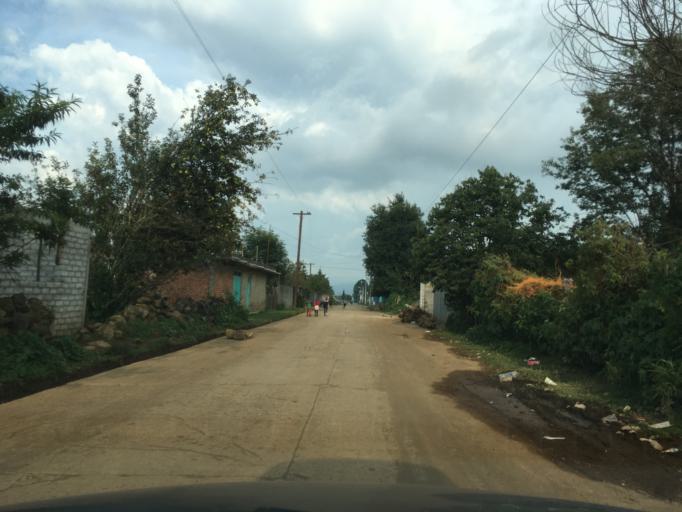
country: MX
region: Michoacan
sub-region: Patzcuaro
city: Santa Maria Huiramangaro (San Juan Tumbio)
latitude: 19.5135
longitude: -101.7647
